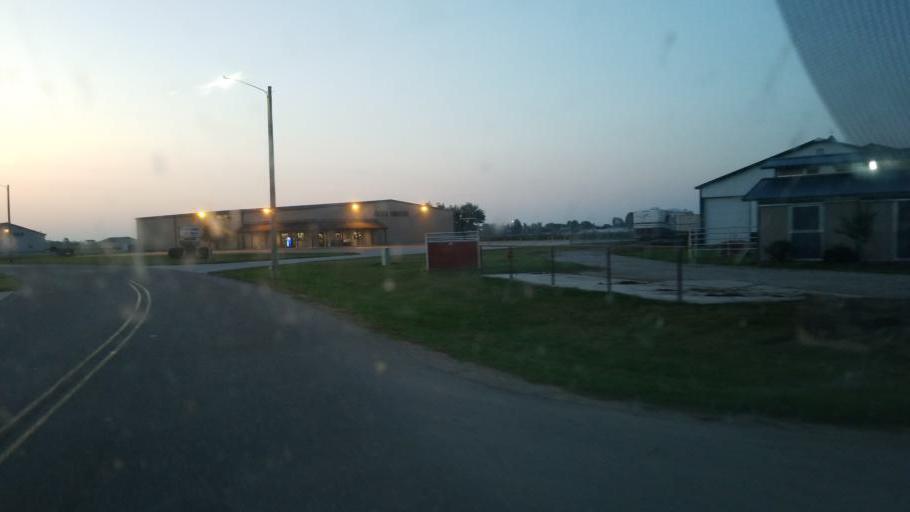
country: US
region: Indiana
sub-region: Elkhart County
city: Middlebury
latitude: 41.6848
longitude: -85.5791
